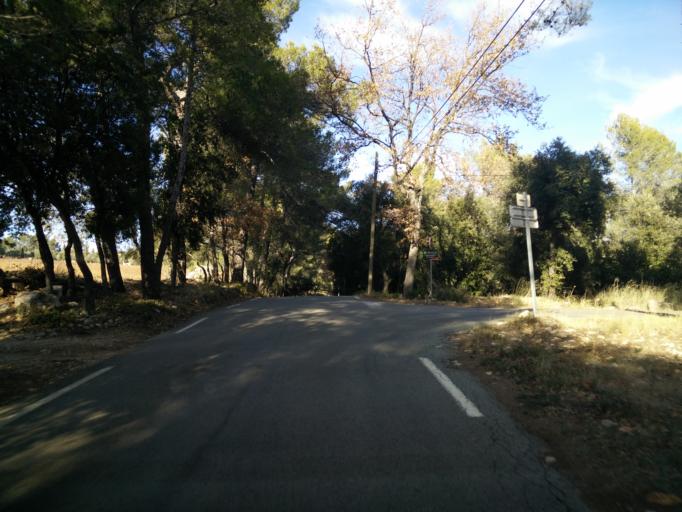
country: FR
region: Provence-Alpes-Cote d'Azur
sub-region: Departement du Var
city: Taradeau
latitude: 43.4681
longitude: 6.4319
